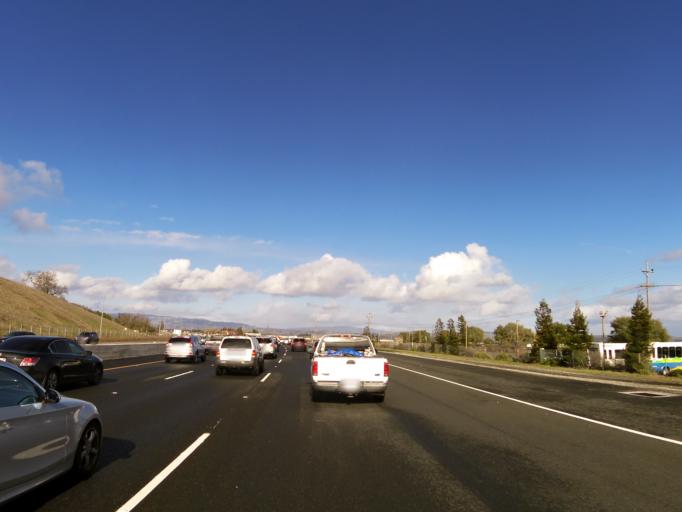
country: US
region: California
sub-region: Marin County
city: Novato
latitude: 38.1294
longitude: -122.5644
